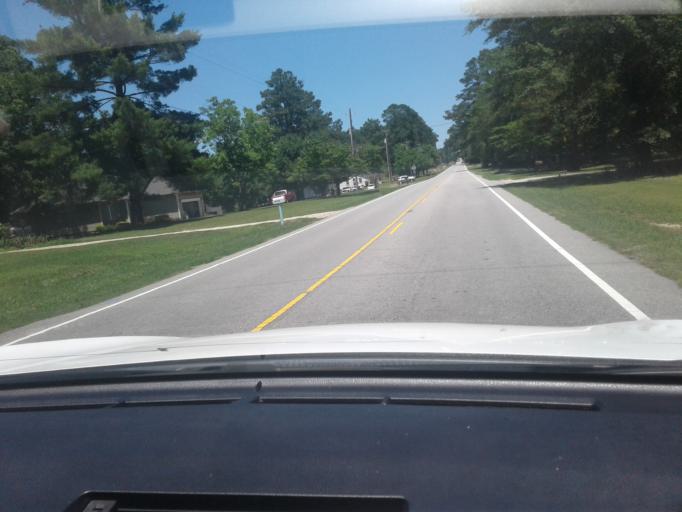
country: US
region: North Carolina
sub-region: Harnett County
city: Lillington
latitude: 35.3825
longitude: -78.8434
